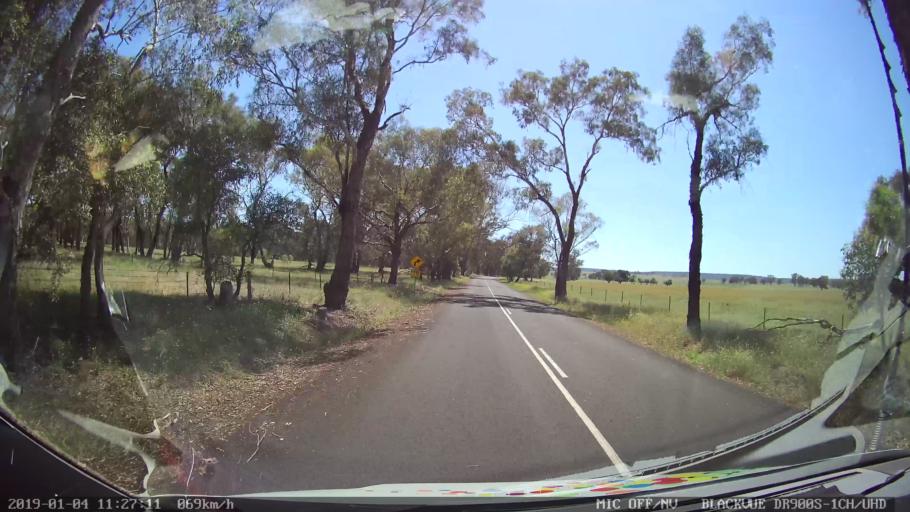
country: AU
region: New South Wales
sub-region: Cabonne
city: Molong
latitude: -33.1104
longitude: 148.7599
